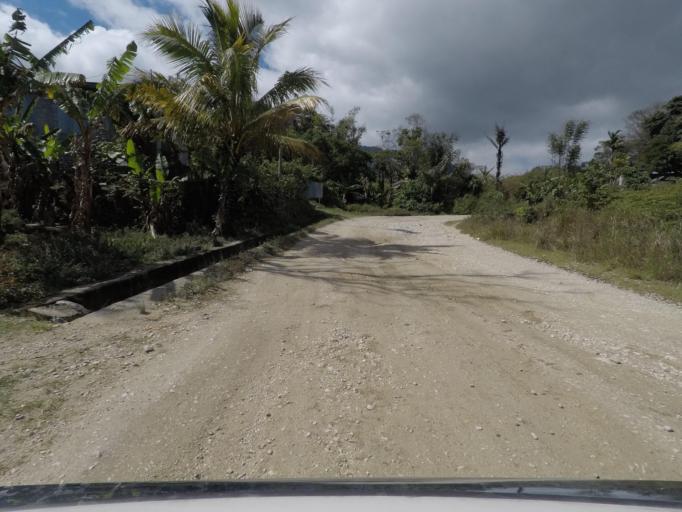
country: TL
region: Baucau
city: Venilale
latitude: -8.6817
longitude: 126.3726
